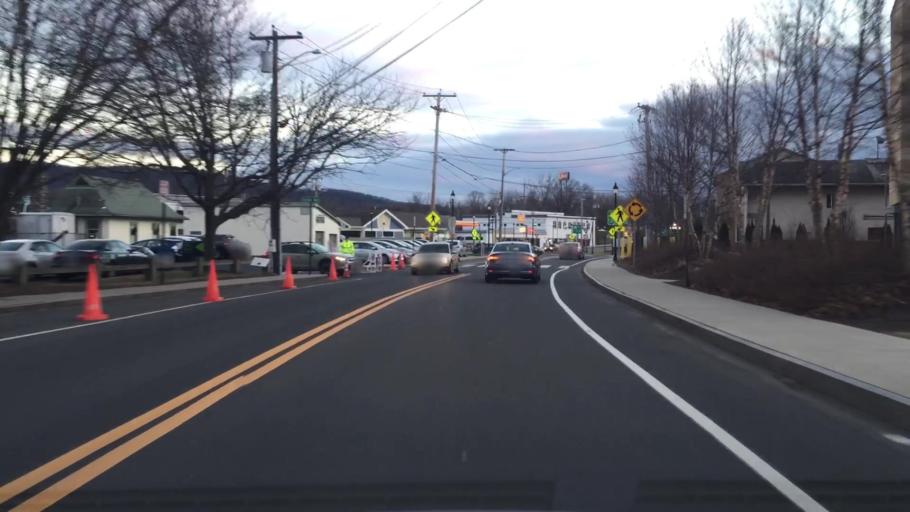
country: US
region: Massachusetts
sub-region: Hampshire County
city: Northampton
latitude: 42.3125
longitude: -72.6255
